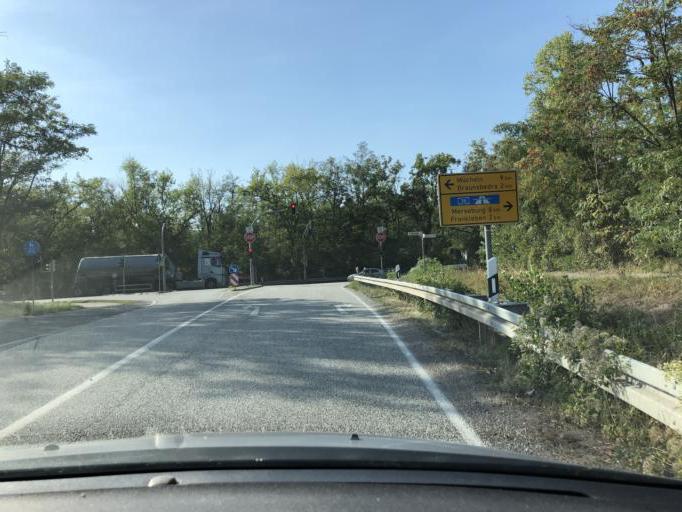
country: DE
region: Saxony-Anhalt
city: Grosskayna
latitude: 51.2938
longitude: 11.9162
